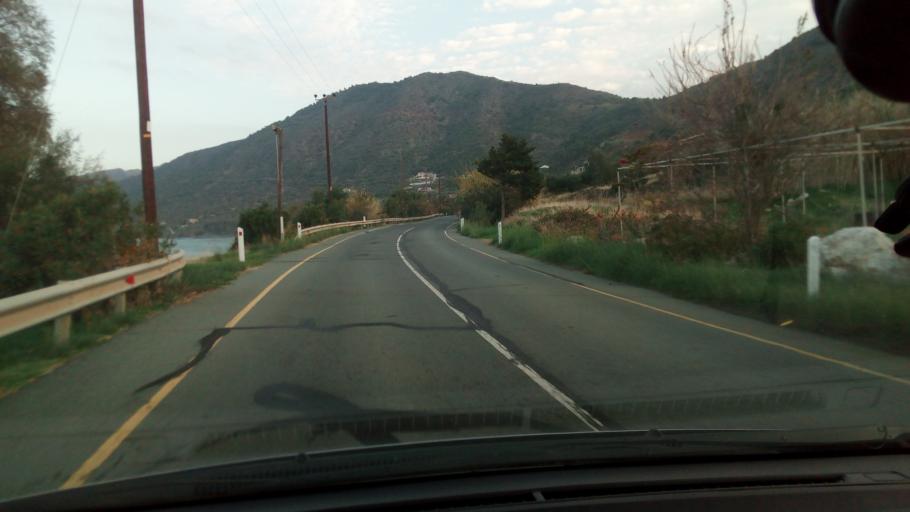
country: CY
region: Lefkosia
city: Kato Pyrgos
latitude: 35.1720
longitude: 32.5556
